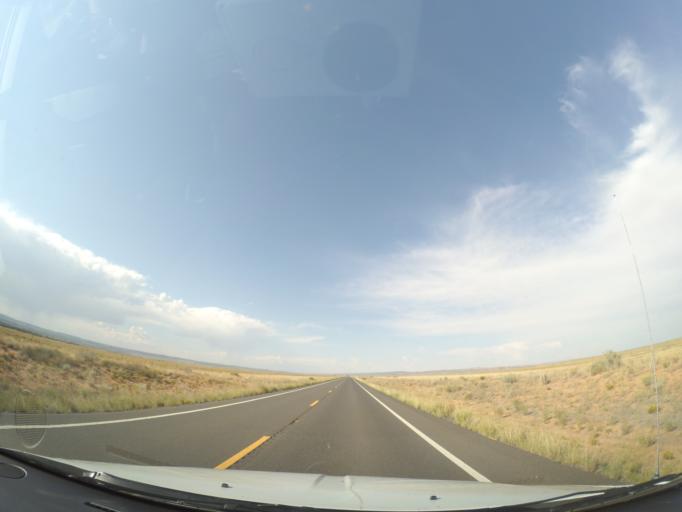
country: US
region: Arizona
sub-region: Coconino County
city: Tuba City
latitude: 36.3652
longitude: -111.4225
